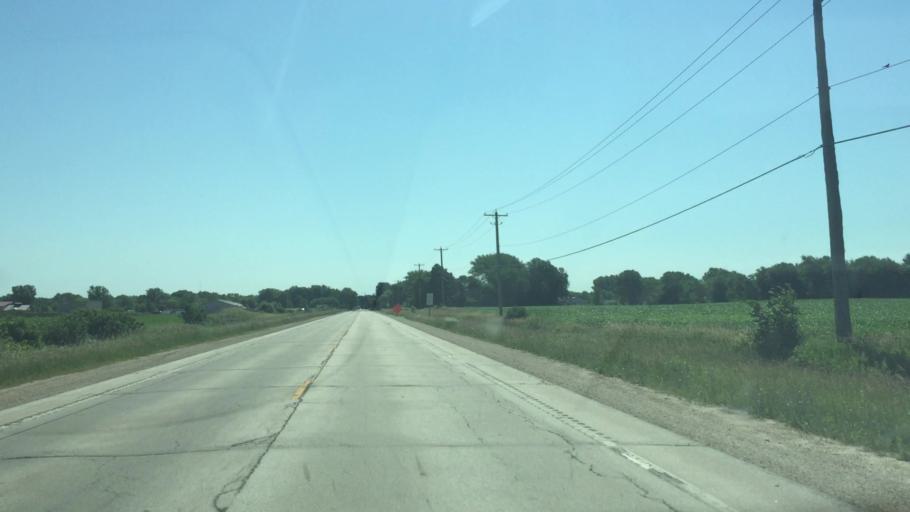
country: US
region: Wisconsin
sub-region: Calumet County
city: Hilbert
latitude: 44.1401
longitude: -88.1782
